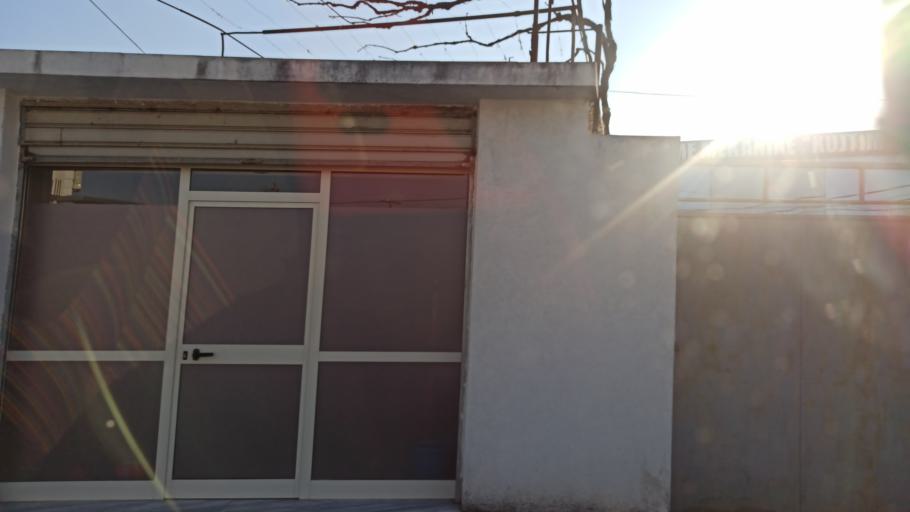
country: AL
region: Shkoder
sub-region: Rrethi i Shkodres
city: Shkoder
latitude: 42.0774
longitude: 19.5020
